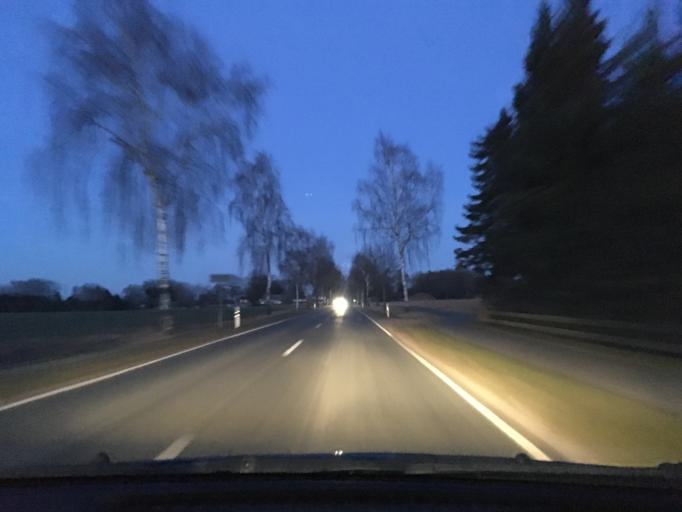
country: DE
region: Lower Saxony
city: Hemslingen
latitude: 53.0990
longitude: 9.6650
